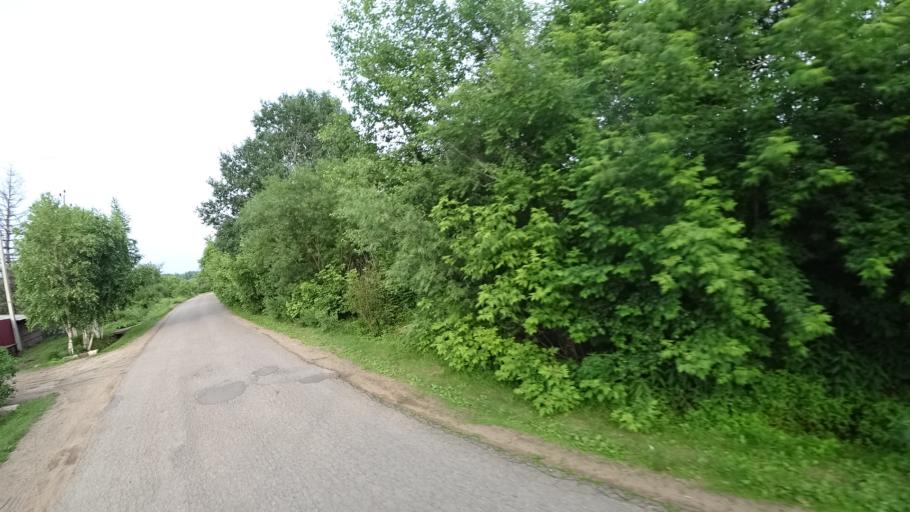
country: RU
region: Primorskiy
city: Novosysoyevka
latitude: 44.2445
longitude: 133.3676
